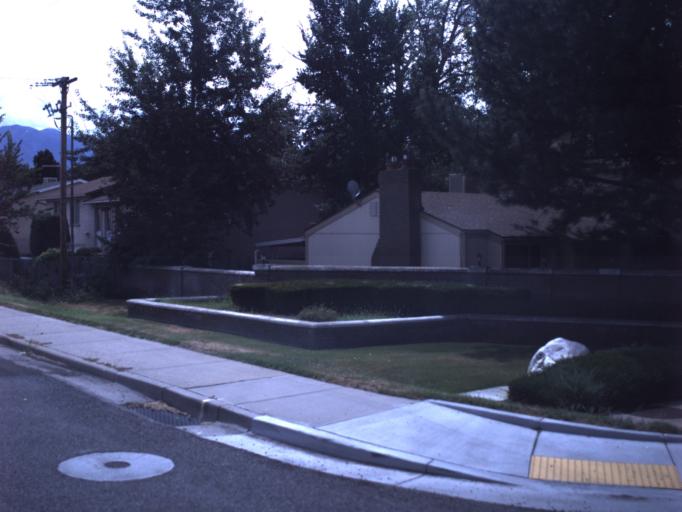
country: US
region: Utah
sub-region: Davis County
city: Hill Air Force Bace
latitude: 41.1035
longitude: -111.9946
